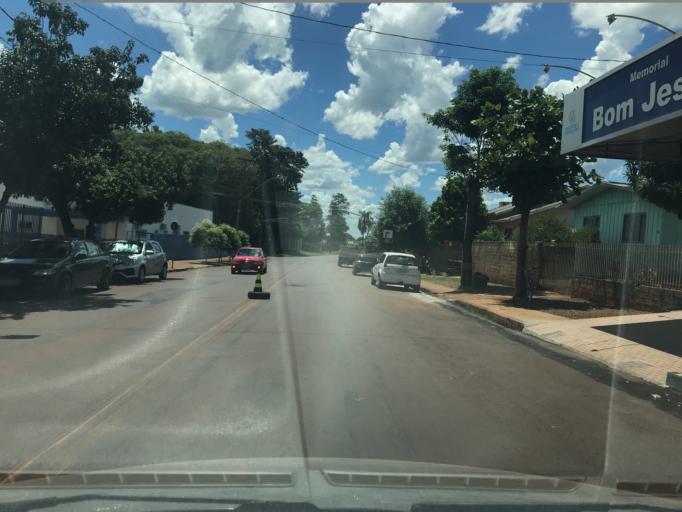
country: BR
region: Parana
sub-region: Palotina
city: Palotina
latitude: -24.2806
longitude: -53.8482
